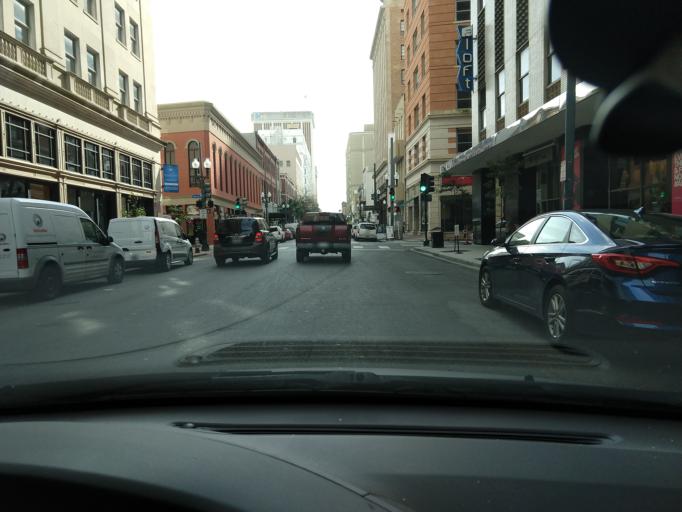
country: US
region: Louisiana
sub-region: Orleans Parish
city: New Orleans
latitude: 29.9528
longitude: -90.0722
